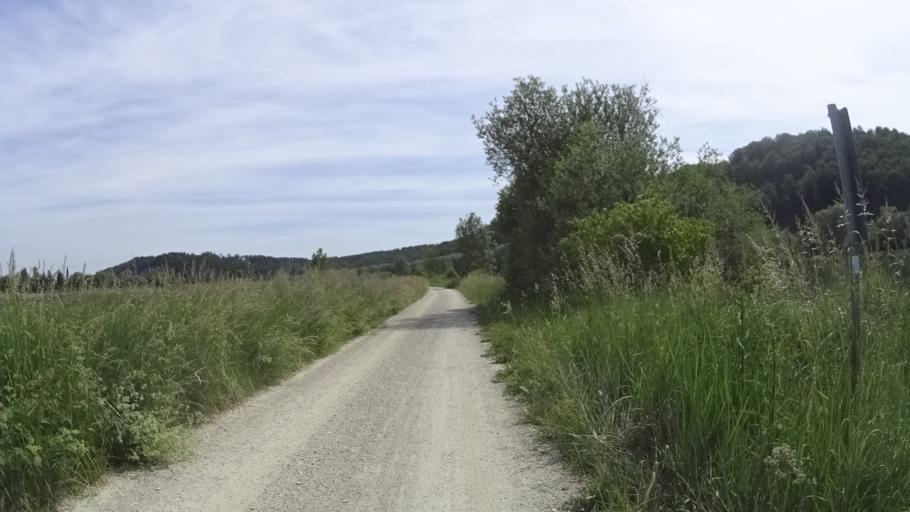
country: DE
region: Bavaria
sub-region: Lower Bavaria
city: Saal
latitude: 48.9051
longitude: 11.9577
